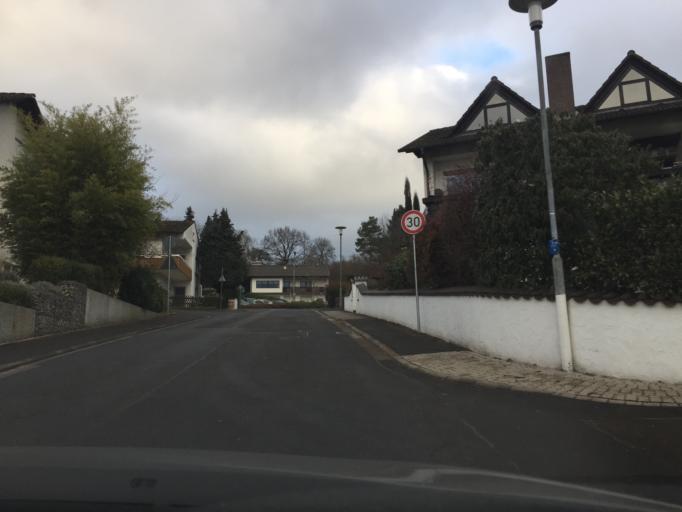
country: DE
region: Bavaria
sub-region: Regierungsbezirk Unterfranken
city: Goldbach
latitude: 49.9983
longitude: 9.1717
